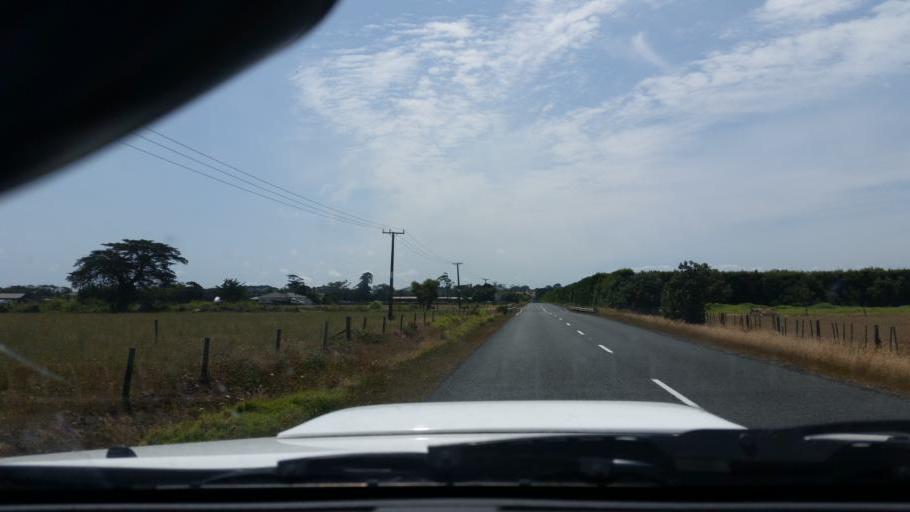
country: NZ
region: Northland
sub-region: Kaipara District
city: Dargaville
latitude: -36.0498
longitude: 173.9288
